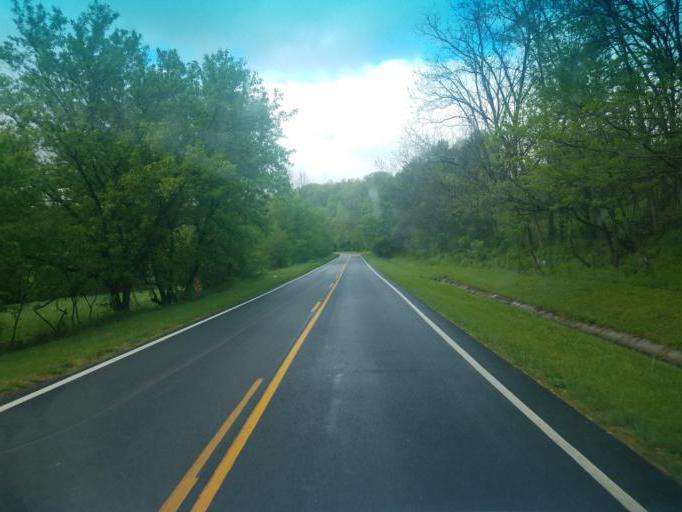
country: US
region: Virginia
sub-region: Washington County
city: Emory
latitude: 36.6653
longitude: -81.8048
